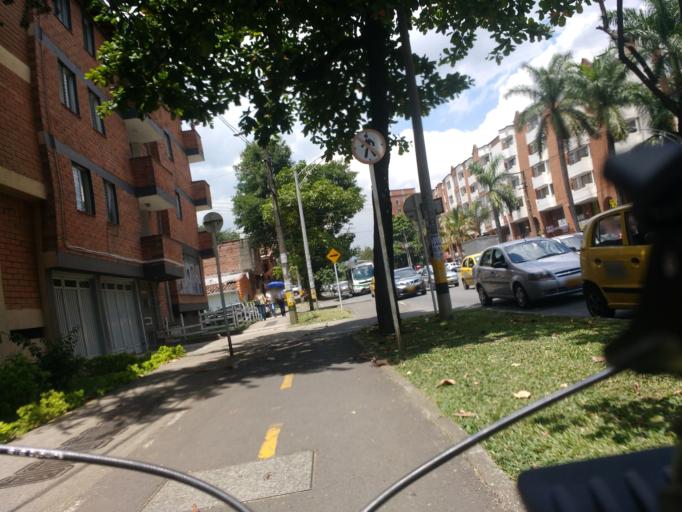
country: CO
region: Antioquia
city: Medellin
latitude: 6.2307
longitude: -75.5915
